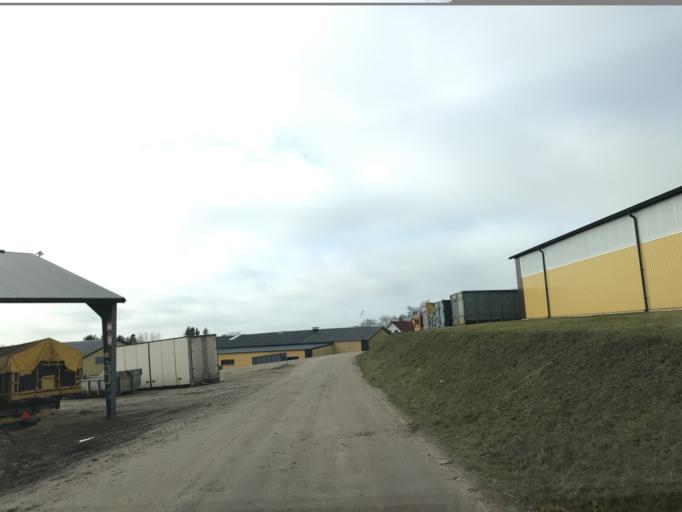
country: SE
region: Skane
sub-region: Svalovs Kommun
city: Teckomatorp
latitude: 55.8269
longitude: 13.0715
